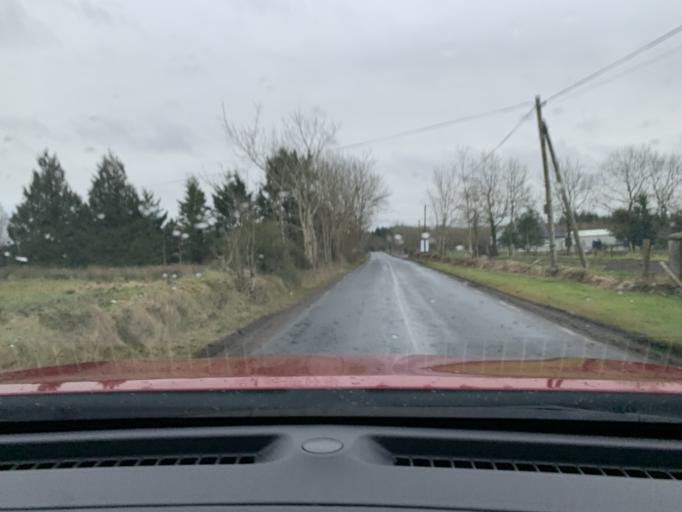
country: IE
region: Connaught
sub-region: Roscommon
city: Boyle
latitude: 53.9880
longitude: -8.3434
